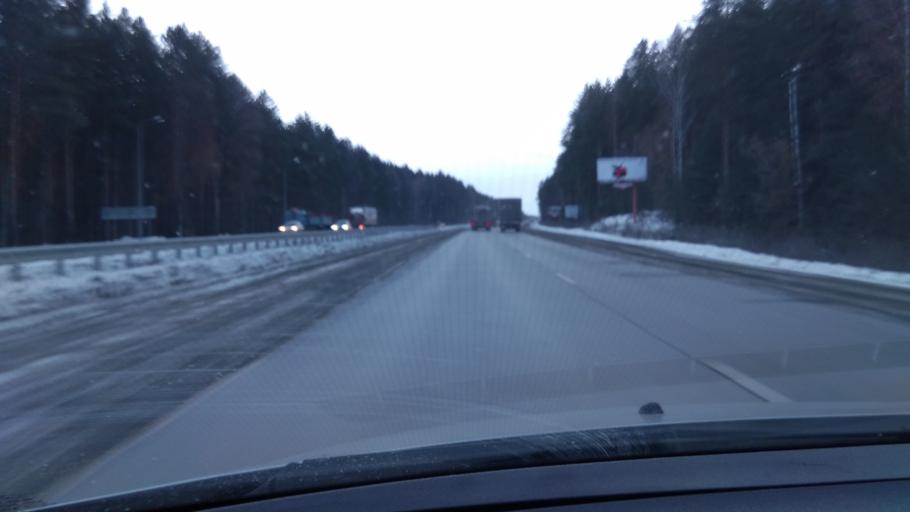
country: RU
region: Sverdlovsk
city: Sysert'
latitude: 56.5717
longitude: 60.8609
